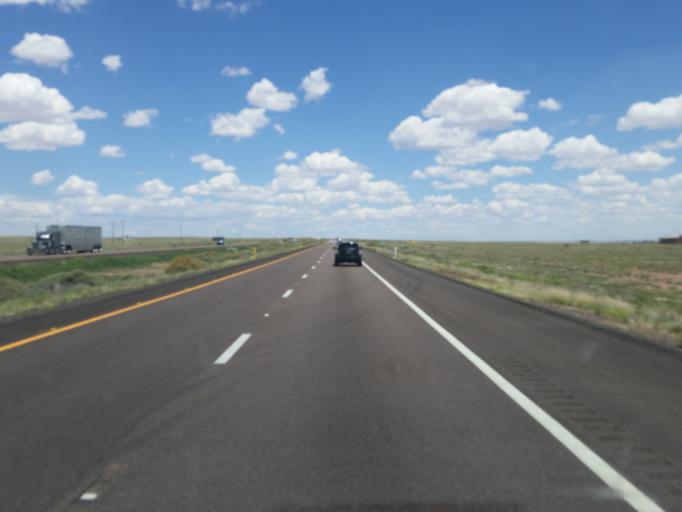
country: US
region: Arizona
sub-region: Navajo County
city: Holbrook
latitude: 34.9842
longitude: -110.0341
